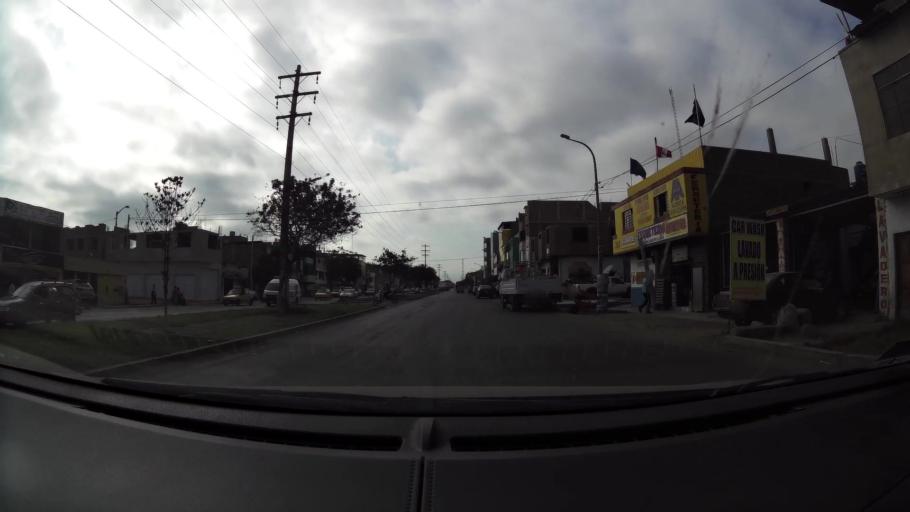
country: PE
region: La Libertad
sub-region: Provincia de Trujillo
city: La Esperanza
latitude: -8.0825
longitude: -79.0431
